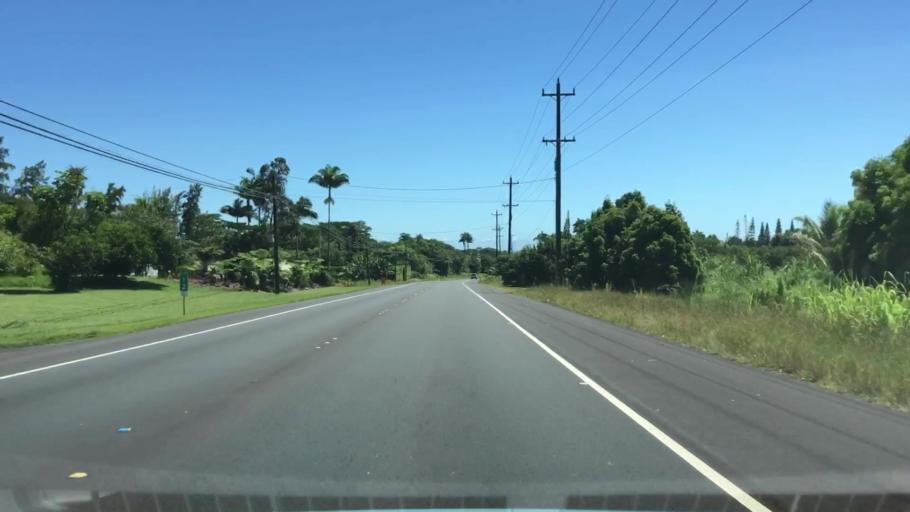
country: US
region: Hawaii
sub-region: Hawaii County
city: Mountain View
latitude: 19.5704
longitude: -155.0793
